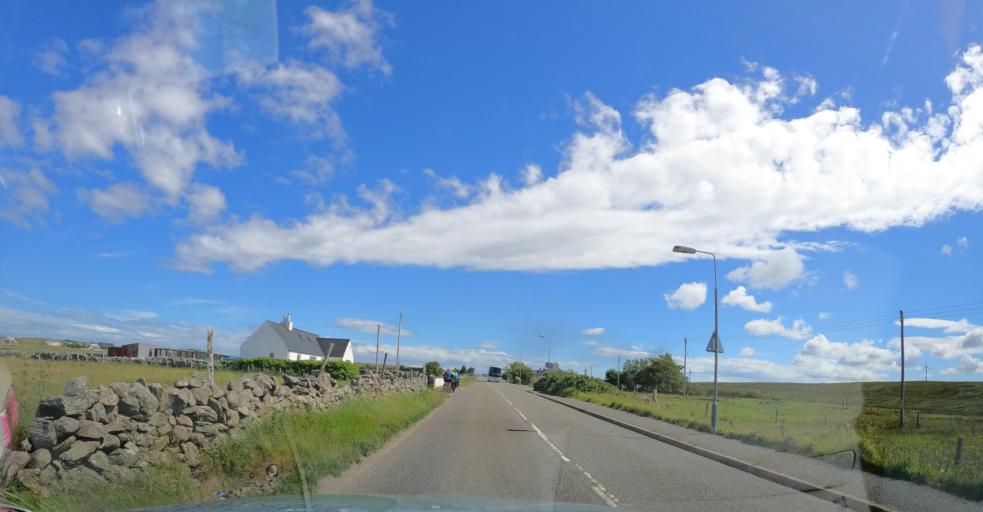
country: GB
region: Scotland
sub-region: Eilean Siar
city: Isle of Lewis
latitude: 58.3486
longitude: -6.5181
